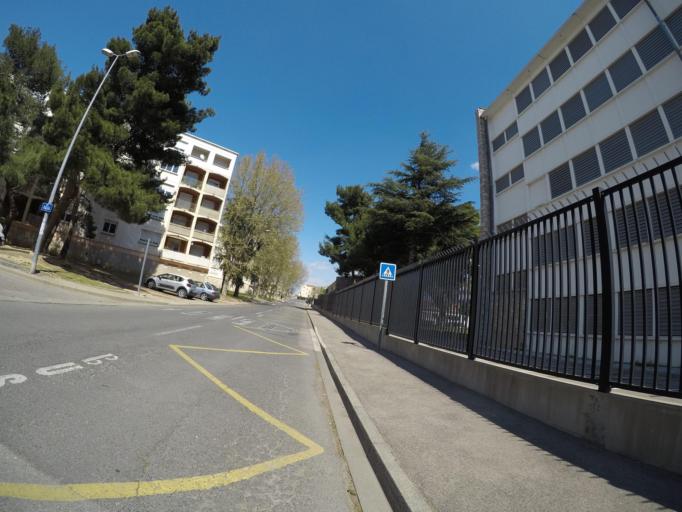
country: FR
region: Languedoc-Roussillon
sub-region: Departement des Pyrenees-Orientales
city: Perpignan
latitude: 42.6927
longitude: 2.9090
